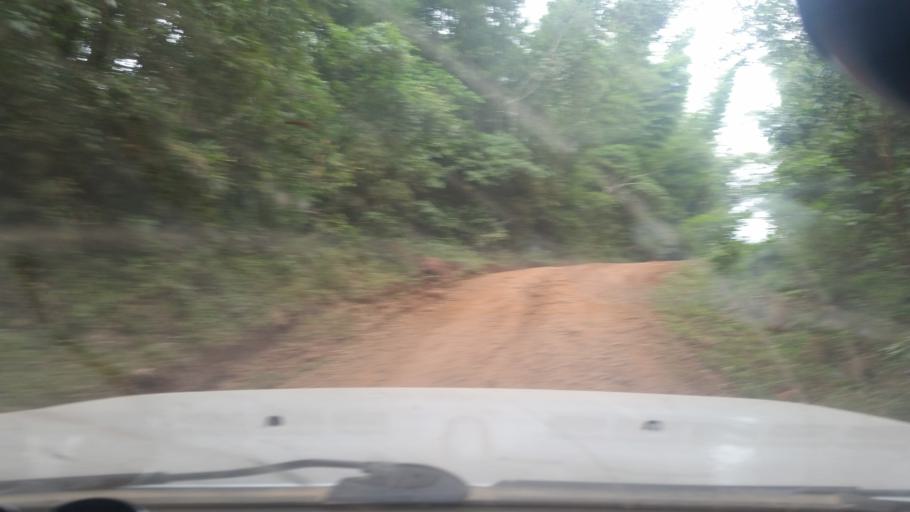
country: PY
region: Guaira
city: Independencia
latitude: -25.8066
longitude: -56.2728
